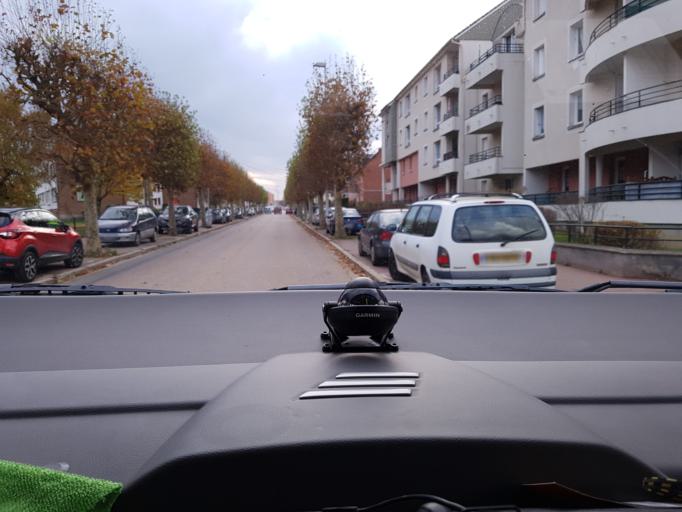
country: FR
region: Haute-Normandie
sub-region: Departement de la Seine-Maritime
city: Rouxmesnil-Bouteilles
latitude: 49.9111
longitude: 1.0682
